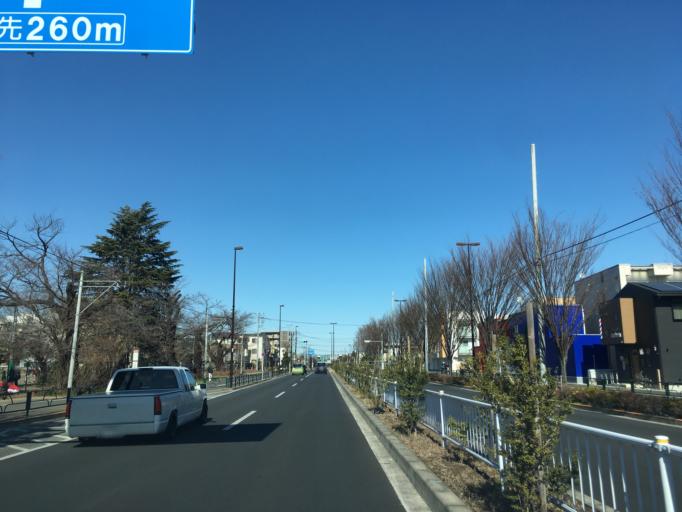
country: JP
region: Tokyo
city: Kamirenjaku
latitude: 35.6930
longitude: 139.5505
